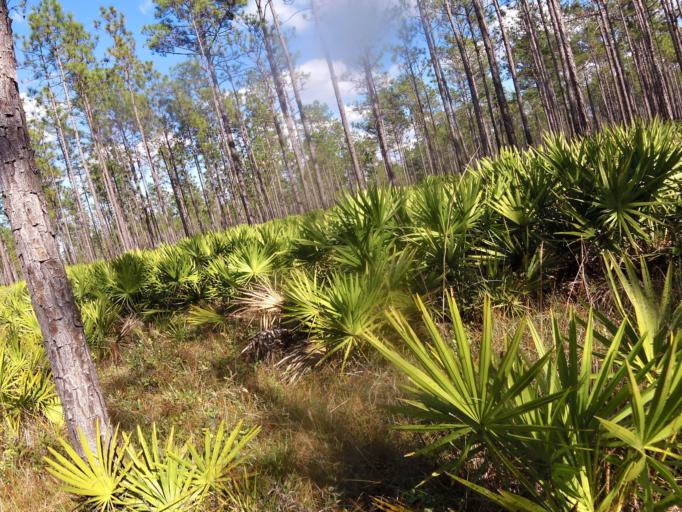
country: US
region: Florida
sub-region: Clay County
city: Middleburg
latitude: 30.1349
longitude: -81.9646
